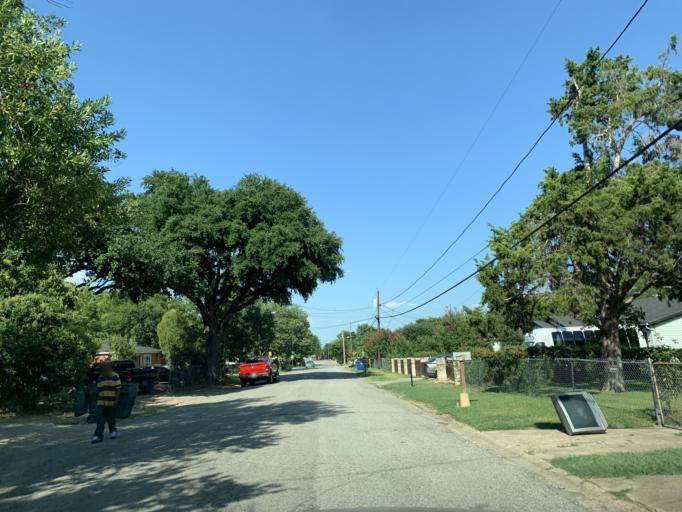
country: US
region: Texas
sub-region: Dallas County
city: Hutchins
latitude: 32.6555
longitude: -96.7703
